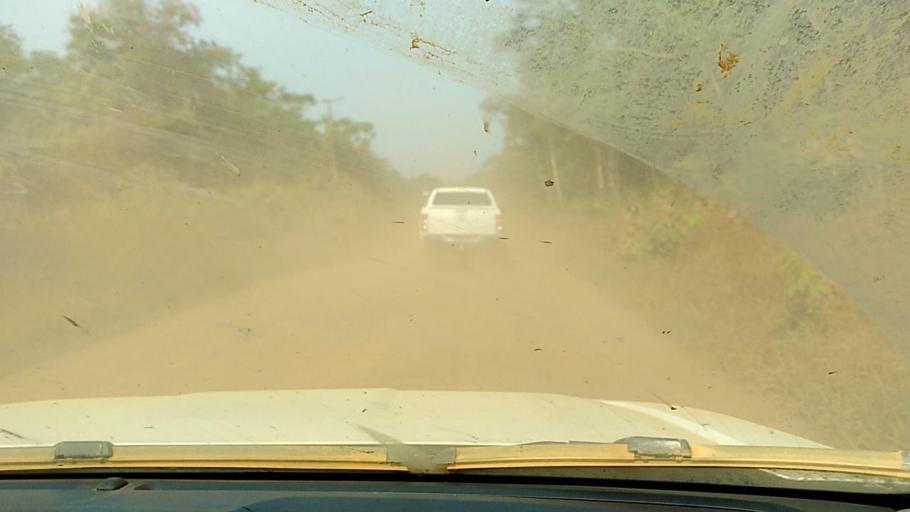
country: BR
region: Rondonia
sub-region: Porto Velho
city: Porto Velho
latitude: -8.8420
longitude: -64.1569
